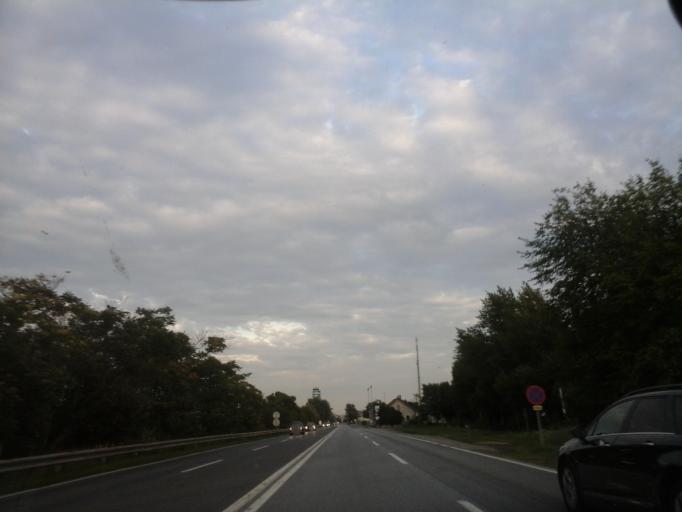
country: AT
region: Lower Austria
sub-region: Politischer Bezirk Wien-Umgebung
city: Rauchenwarth
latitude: 48.1310
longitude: 16.5392
